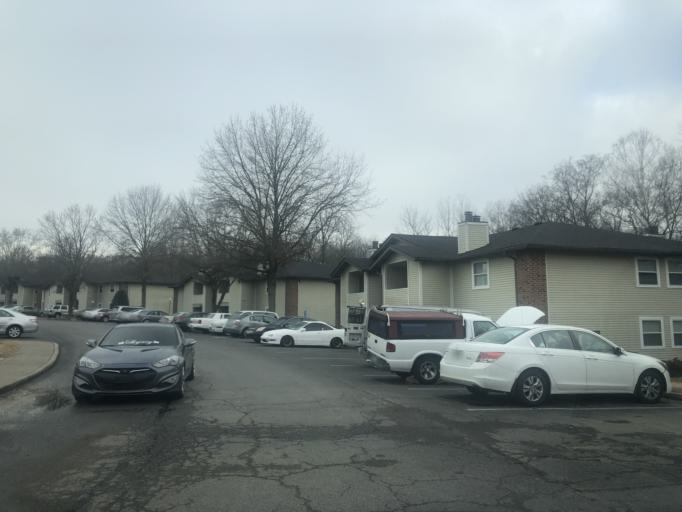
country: US
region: Tennessee
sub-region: Rutherford County
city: La Vergne
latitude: 36.0700
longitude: -86.6429
